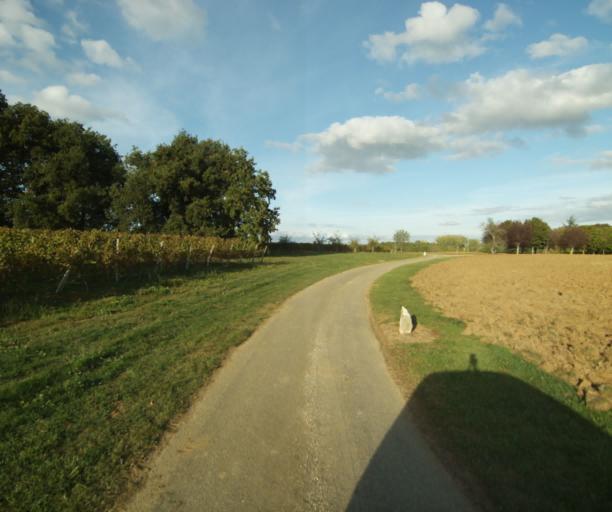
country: FR
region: Midi-Pyrenees
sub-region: Departement du Gers
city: Gondrin
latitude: 43.8920
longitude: 0.2527
